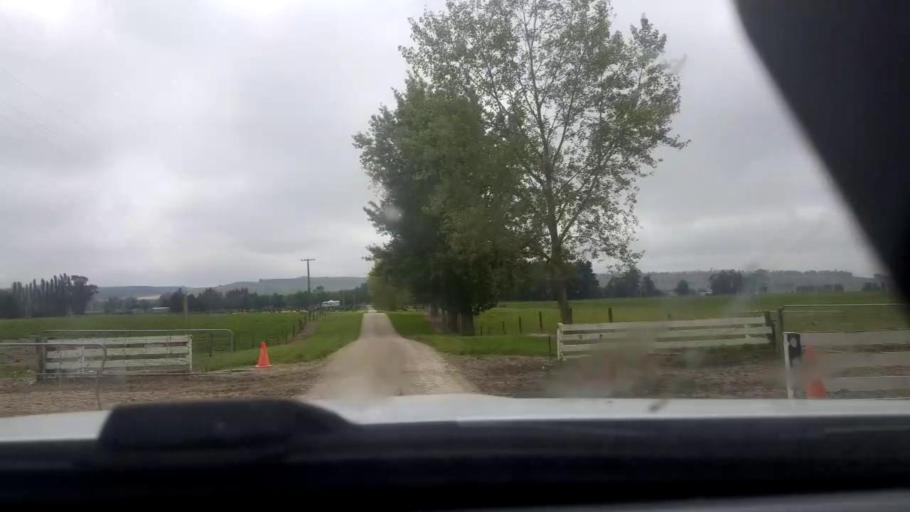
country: NZ
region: Canterbury
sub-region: Timaru District
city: Pleasant Point
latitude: -44.2118
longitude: 171.1095
